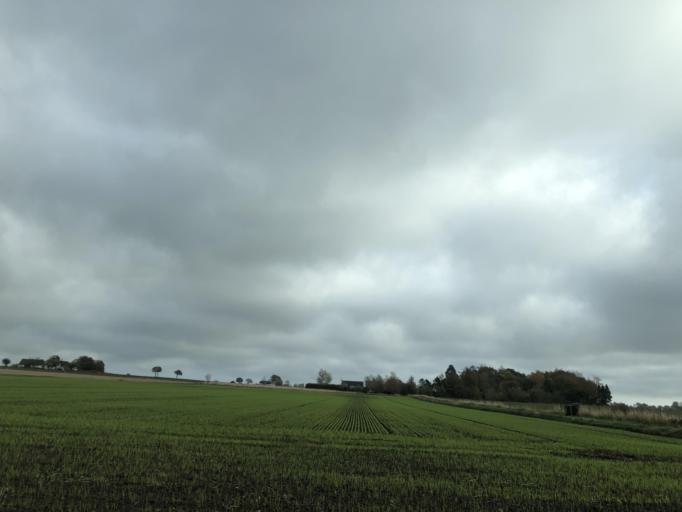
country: SE
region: Skane
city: Smygehamn
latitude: 55.3500
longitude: 13.3152
